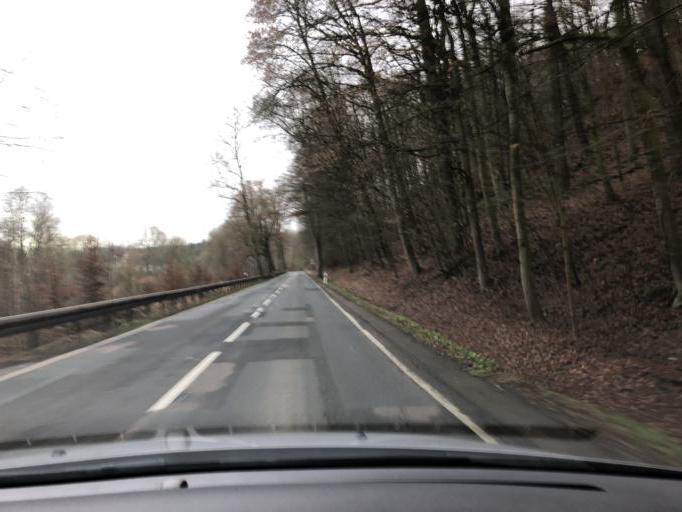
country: DE
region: Saxony
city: Niederstriegis
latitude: 51.0933
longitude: 13.1349
